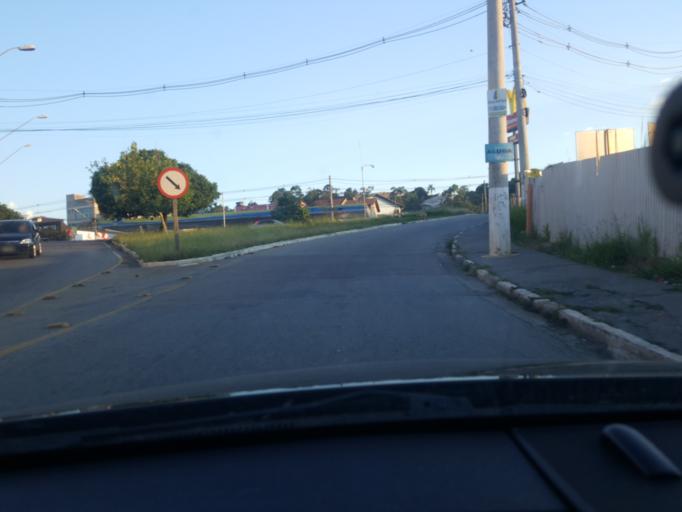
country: BR
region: Sao Paulo
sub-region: Cajamar
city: Cajamar
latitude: -23.4058
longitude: -46.8653
